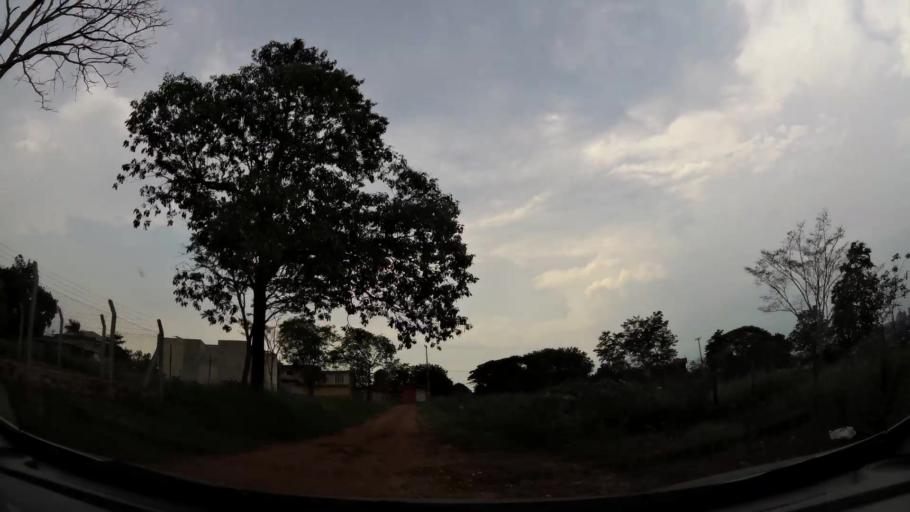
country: BR
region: Parana
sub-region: Foz Do Iguacu
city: Foz do Iguacu
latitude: -25.5381
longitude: -54.6010
